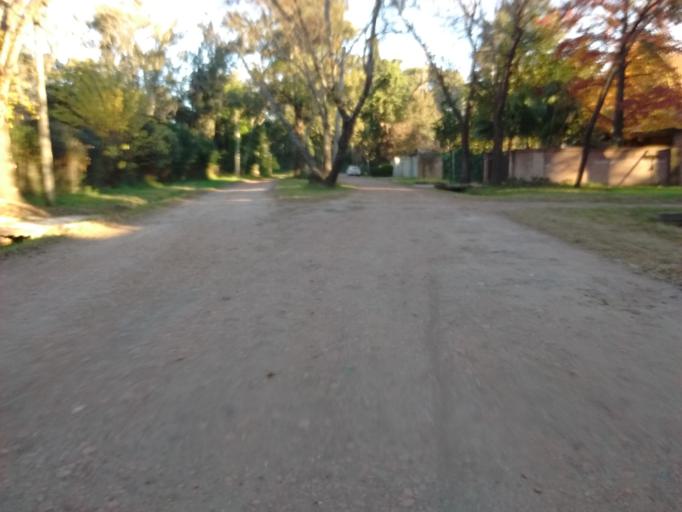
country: AR
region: Santa Fe
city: Funes
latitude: -32.9156
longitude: -60.8328
